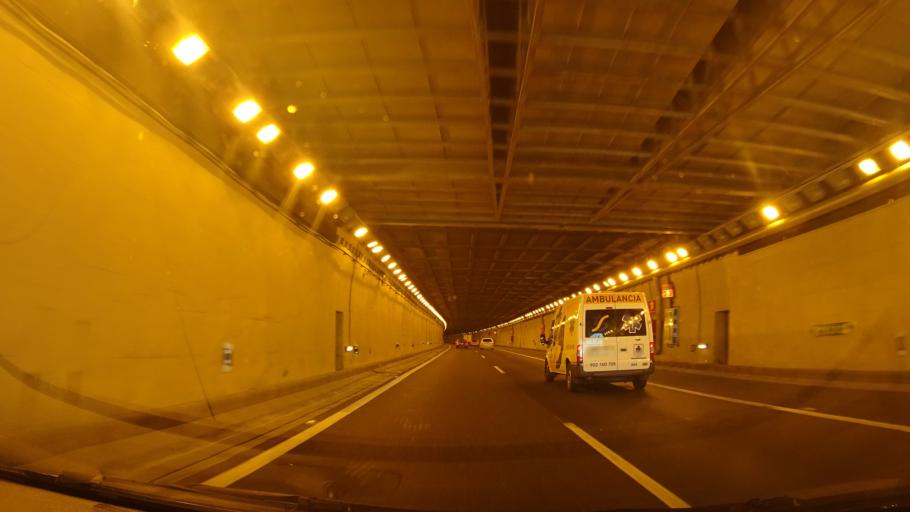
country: ES
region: Madrid
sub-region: Provincia de Madrid
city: Guadarrama
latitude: 40.7002
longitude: -4.1293
